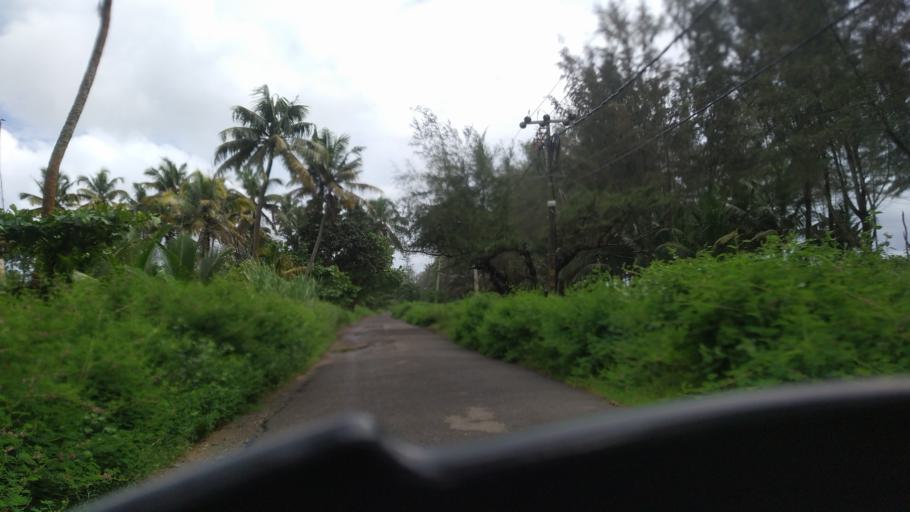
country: IN
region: Kerala
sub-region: Thrissur District
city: Kodungallur
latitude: 10.1238
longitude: 76.1841
